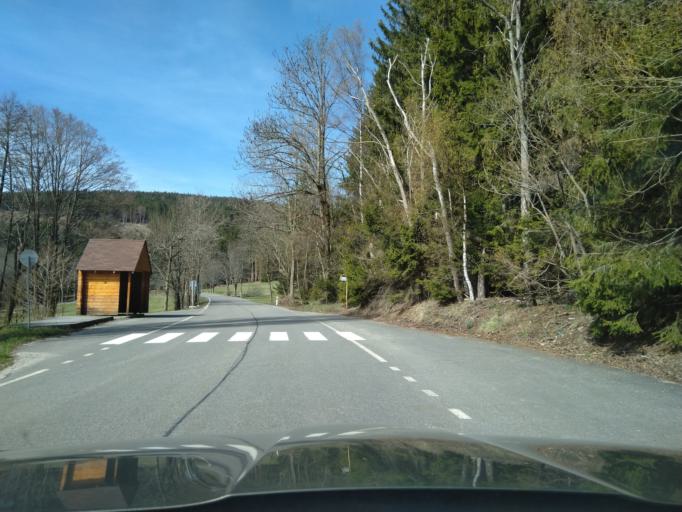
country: CZ
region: Jihocesky
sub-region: Okres Prachatice
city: Stachy
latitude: 49.0910
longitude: 13.6426
